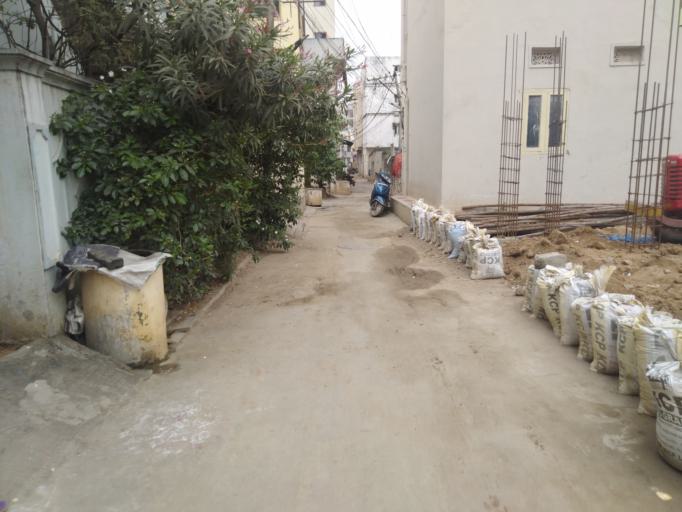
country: IN
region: Telangana
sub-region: Rangareddi
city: Kukatpalli
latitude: 17.4866
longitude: 78.4126
